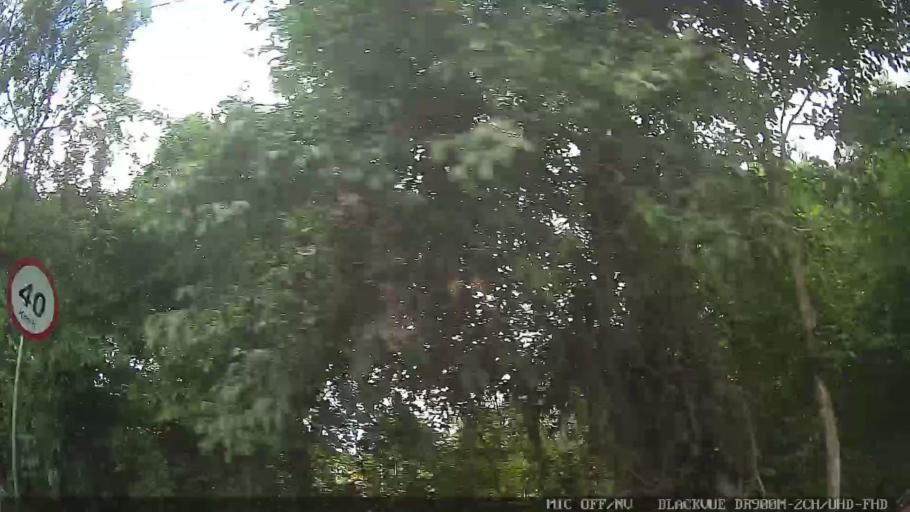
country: BR
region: Sao Paulo
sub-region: Jaguariuna
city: Jaguariuna
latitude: -22.6970
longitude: -47.0091
